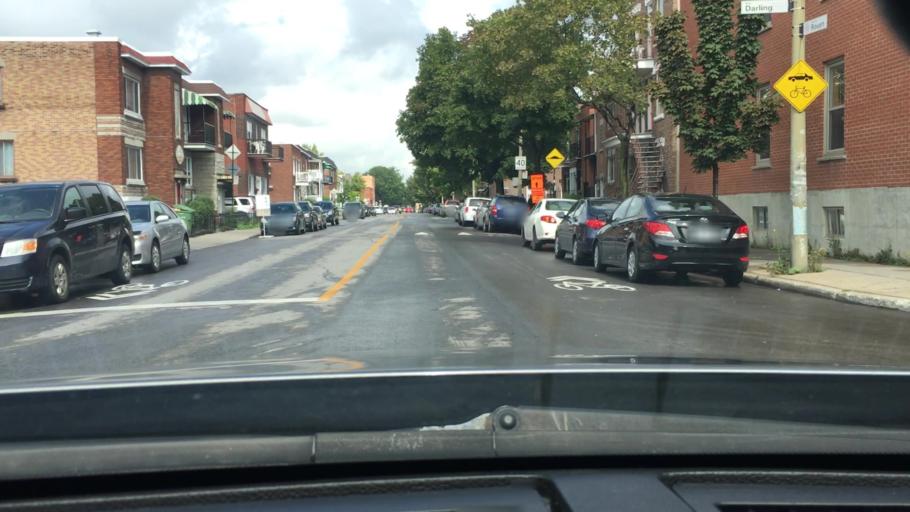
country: CA
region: Quebec
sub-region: Monteregie
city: Longueuil
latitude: 45.5434
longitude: -73.5499
